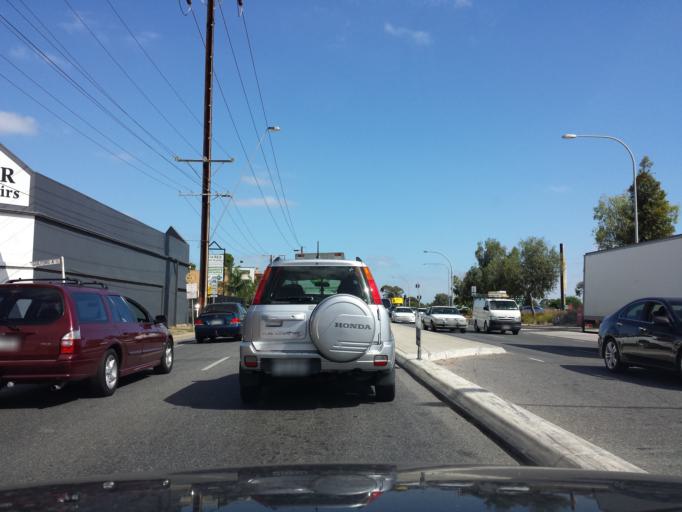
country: AU
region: South Australia
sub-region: Prospect
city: Prospect
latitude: -34.8730
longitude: 138.5840
